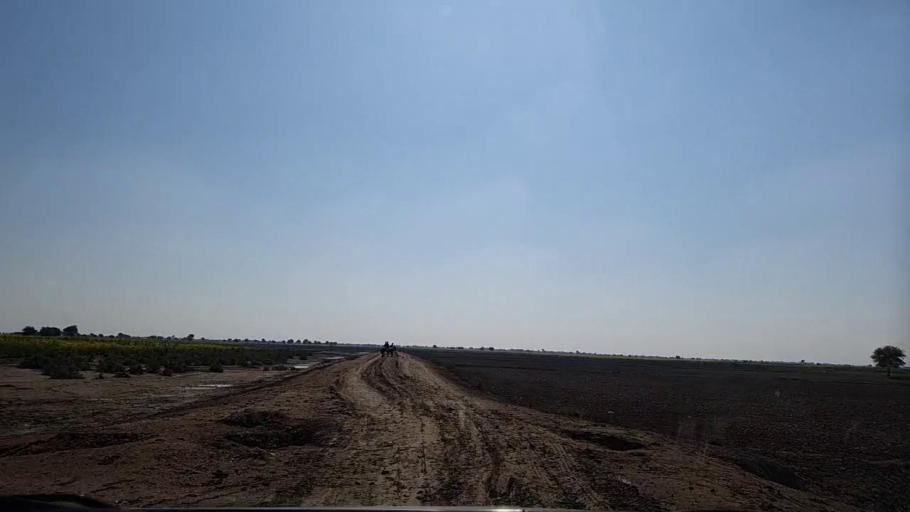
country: PK
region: Sindh
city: Pithoro
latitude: 25.6886
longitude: 69.3557
